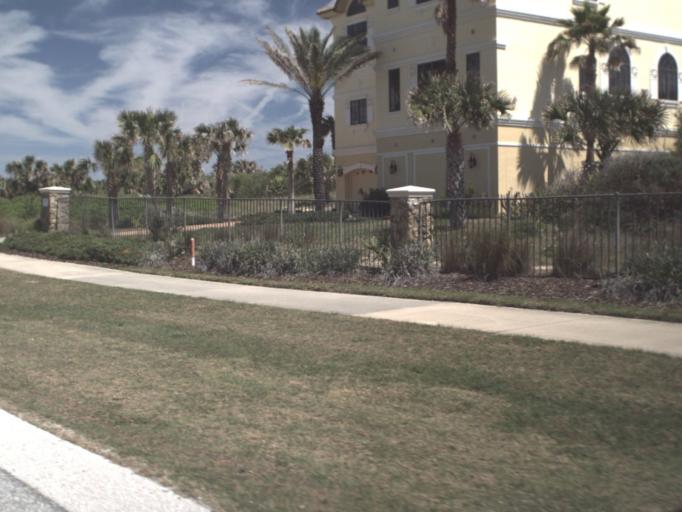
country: US
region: Florida
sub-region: Flagler County
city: Palm Coast
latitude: 29.5587
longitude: -81.1663
